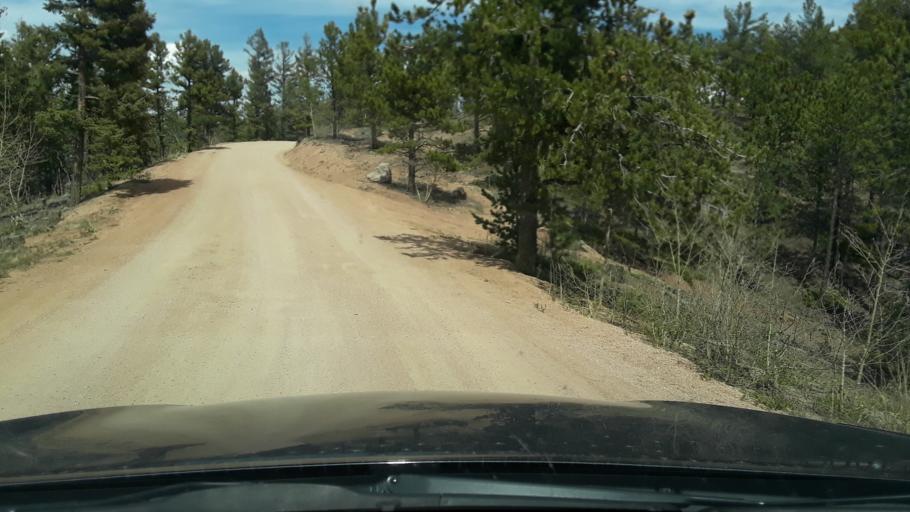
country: US
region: Colorado
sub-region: El Paso County
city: Palmer Lake
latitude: 39.0685
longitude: -104.9561
